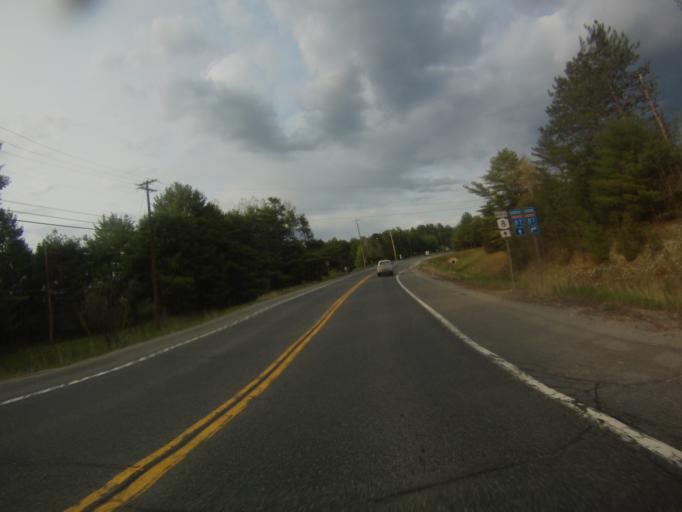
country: US
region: New York
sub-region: Warren County
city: Warrensburg
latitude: 43.6665
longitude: -73.7830
